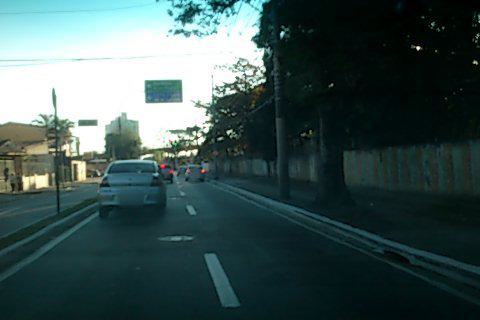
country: BR
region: Sao Paulo
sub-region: Sao Jose Dos Campos
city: Sao Jose dos Campos
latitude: -23.1743
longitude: -45.8873
